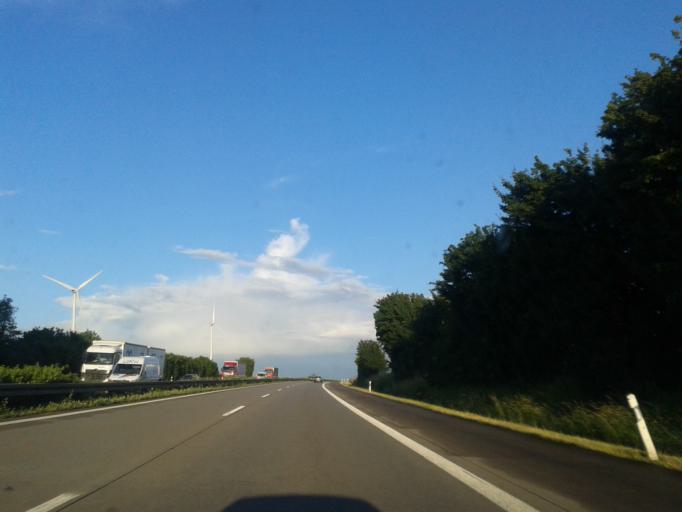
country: DE
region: Saxony
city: Nerchau
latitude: 51.2519
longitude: 12.8364
